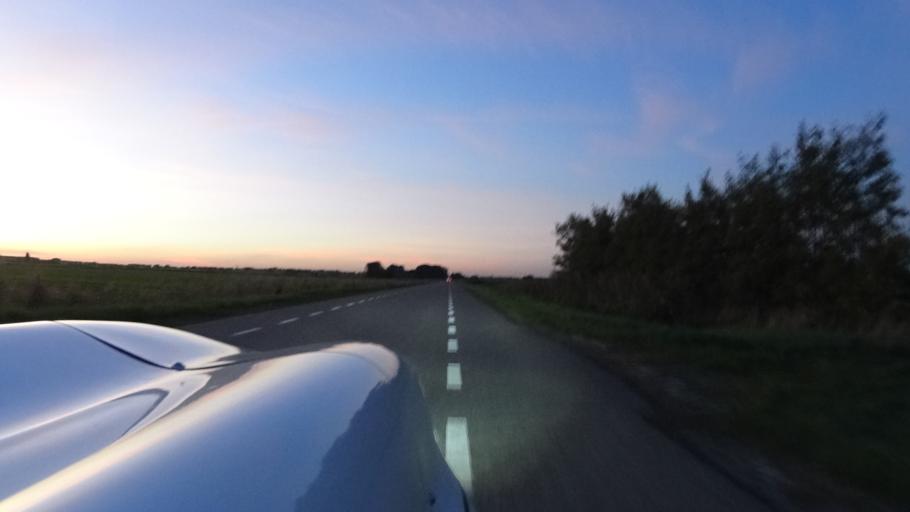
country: NL
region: North Brabant
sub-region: Gemeente Aalburg
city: Aalburg
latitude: 51.7452
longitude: 5.0860
